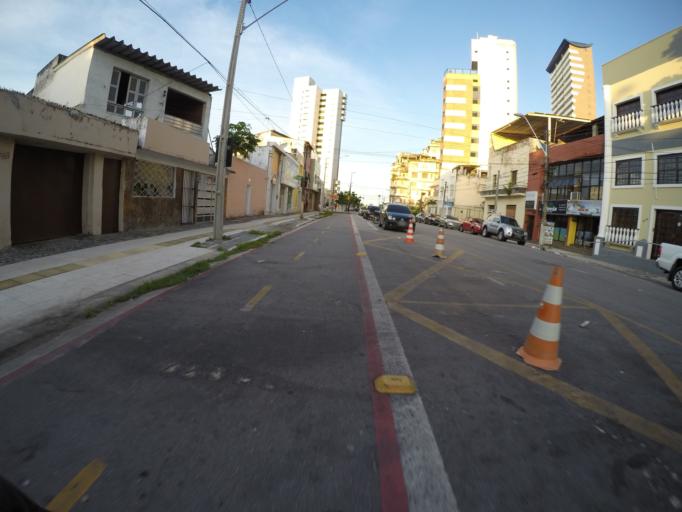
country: BR
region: Ceara
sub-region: Fortaleza
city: Fortaleza
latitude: -3.7201
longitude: -38.5144
